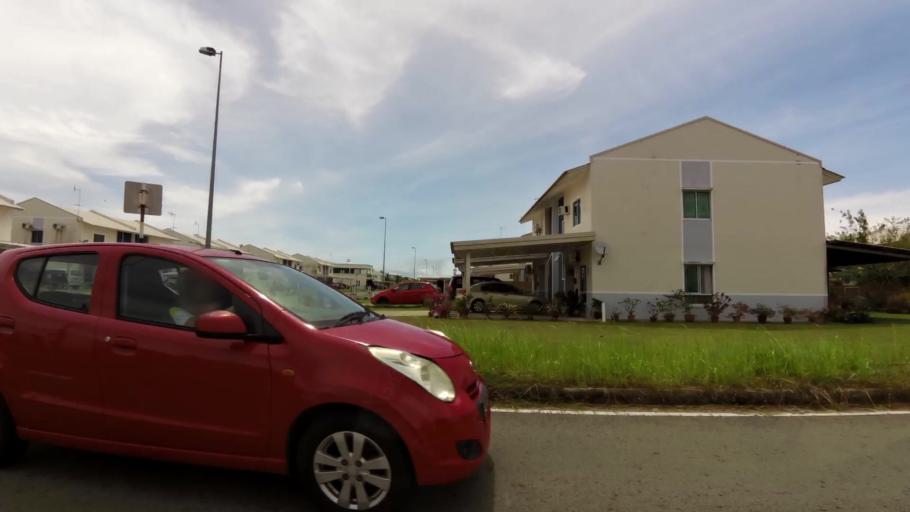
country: BN
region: Belait
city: Kuala Belait
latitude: 4.5887
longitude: 114.2659
